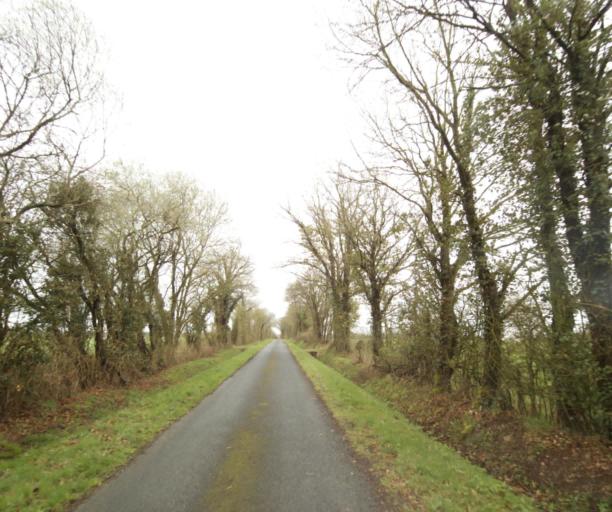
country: FR
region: Pays de la Loire
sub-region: Departement de la Loire-Atlantique
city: Bouvron
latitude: 47.4442
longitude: -1.8492
